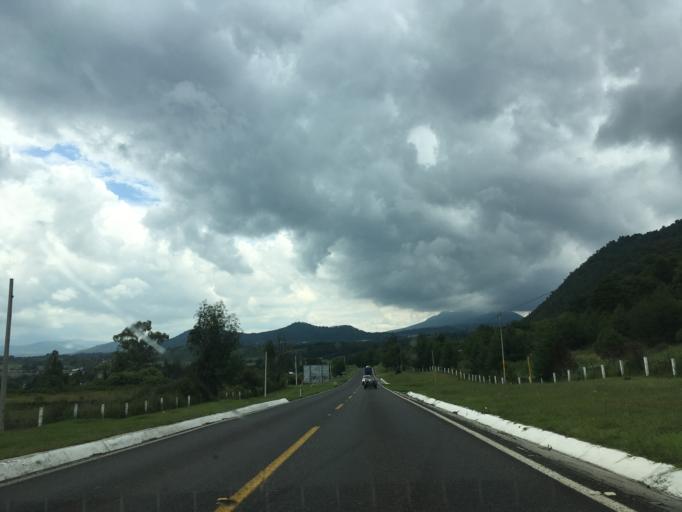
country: MX
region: Michoacan
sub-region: Patzcuaro
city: Santa Ana Chapitiro
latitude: 19.5227
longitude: -101.6564
